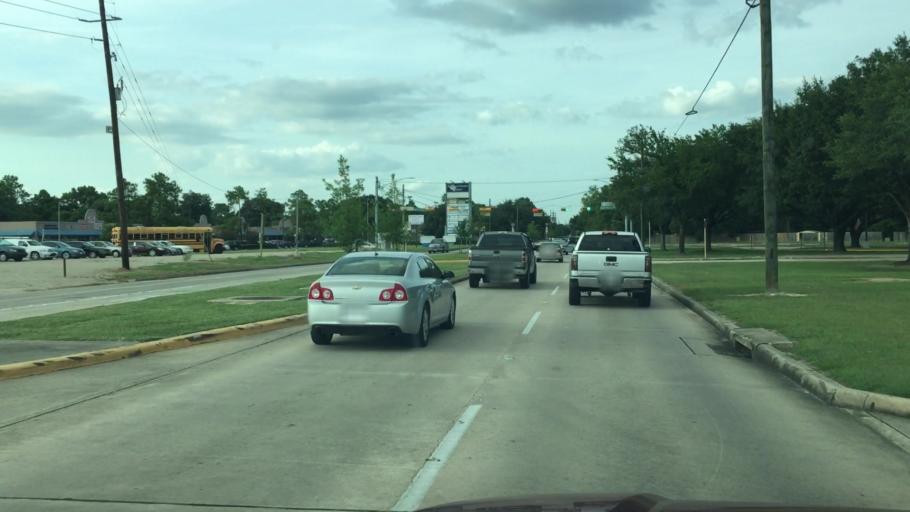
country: US
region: Texas
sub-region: Harris County
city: Hudson
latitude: 29.9719
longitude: -95.4946
